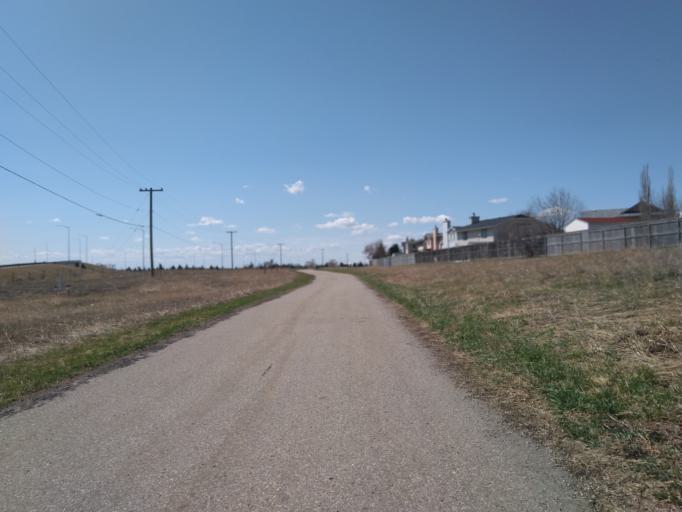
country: CA
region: Alberta
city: Chestermere
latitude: 51.0712
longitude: -113.9232
